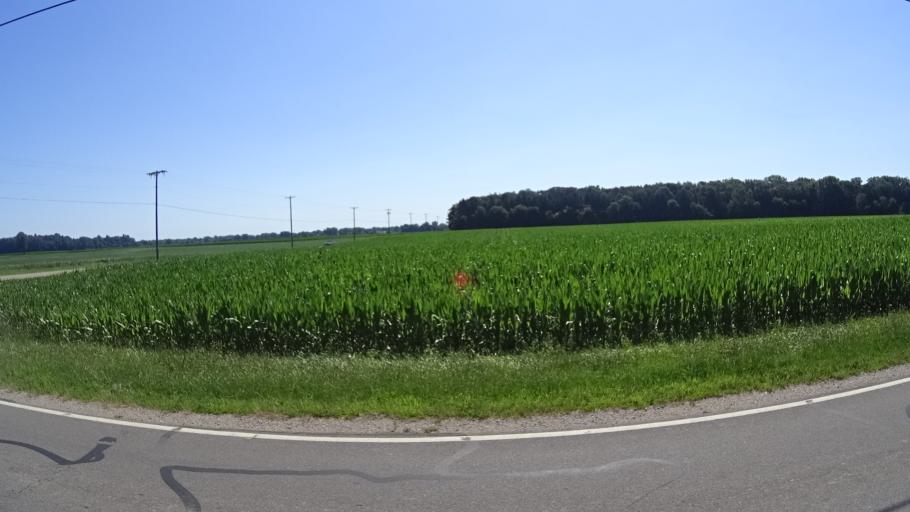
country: US
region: Ohio
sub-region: Erie County
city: Huron
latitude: 41.3767
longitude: -82.5903
